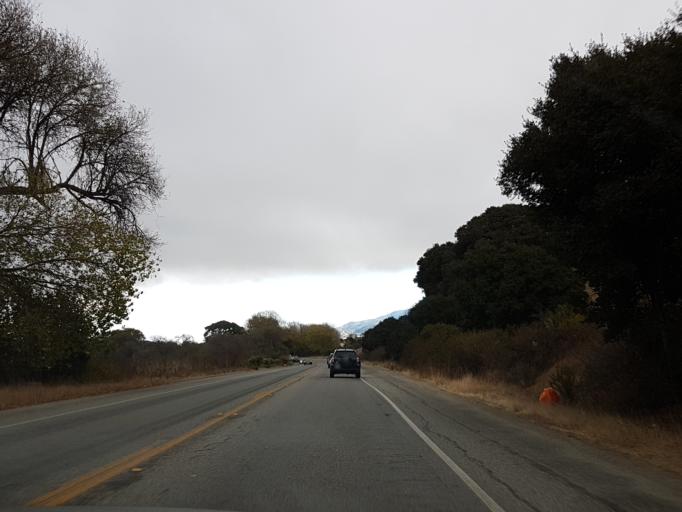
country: US
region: California
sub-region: Monterey County
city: Salinas
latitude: 36.6112
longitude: -121.6526
